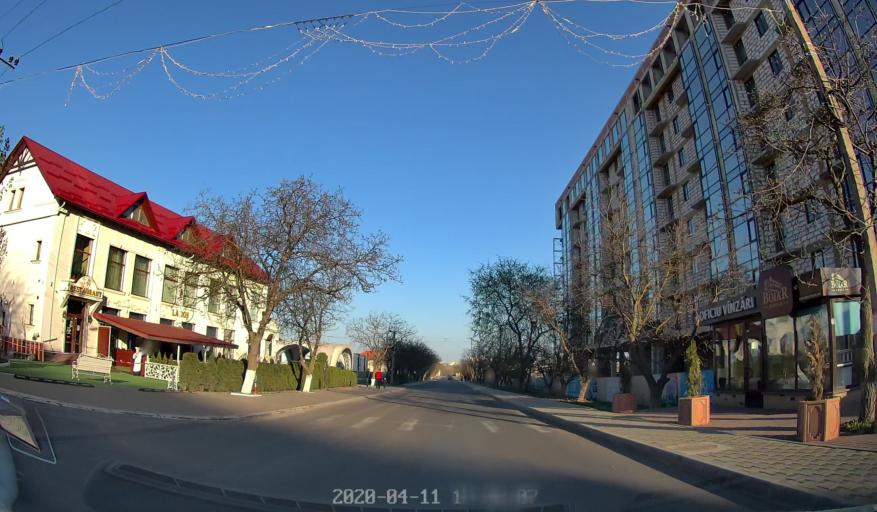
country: MD
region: Chisinau
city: Vatra
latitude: 47.0142
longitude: 28.7518
